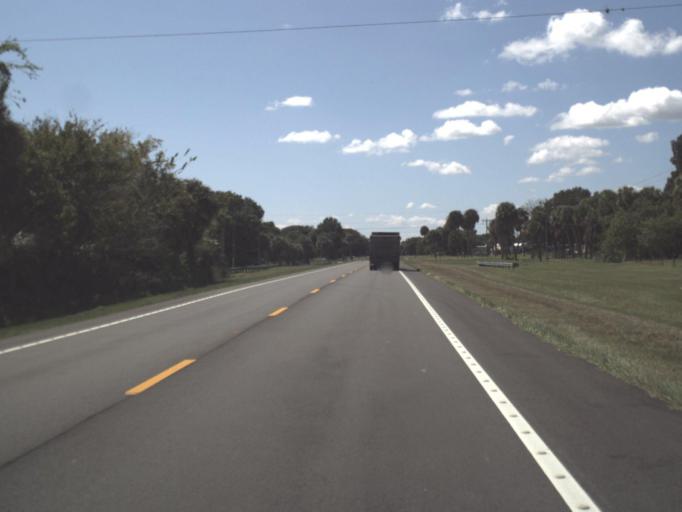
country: US
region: Florida
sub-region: Glades County
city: Moore Haven
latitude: 27.0088
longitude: -81.0399
